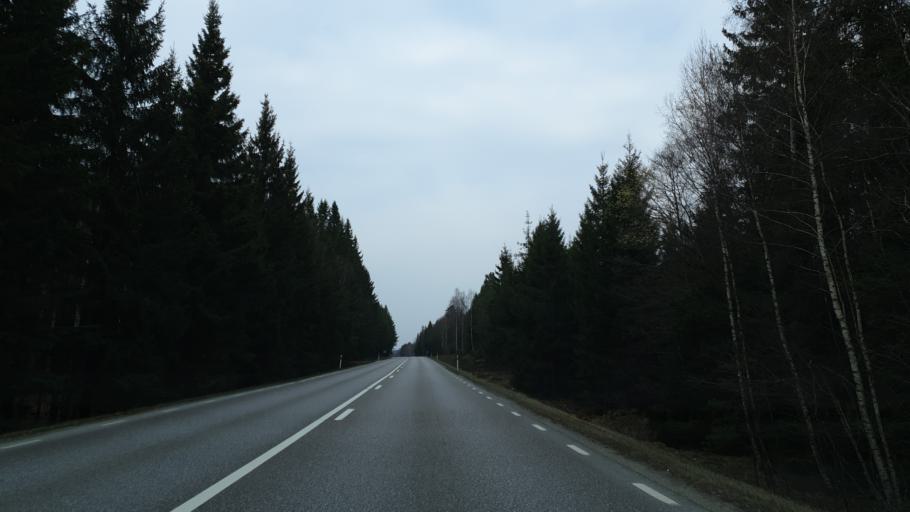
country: SE
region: Vaestra Goetaland
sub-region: Vargarda Kommun
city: Vargarda
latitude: 57.9808
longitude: 12.8134
